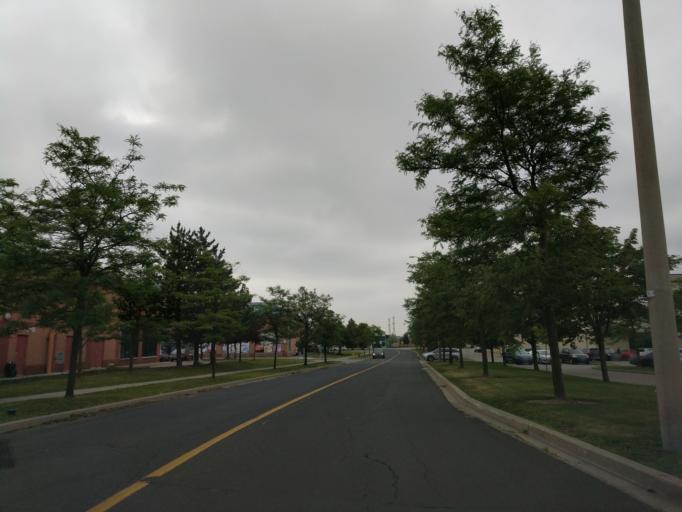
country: CA
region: Ontario
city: Markham
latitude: 43.8493
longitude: -79.3510
